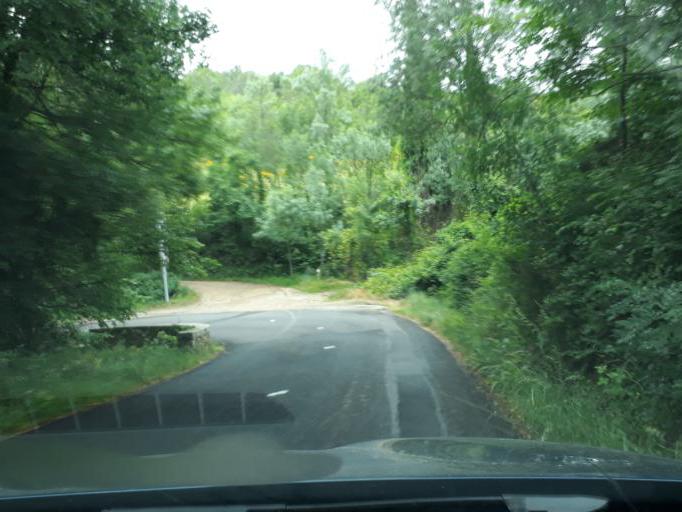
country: FR
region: Languedoc-Roussillon
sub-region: Departement de l'Herault
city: Lodeve
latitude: 43.7616
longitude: 3.3184
